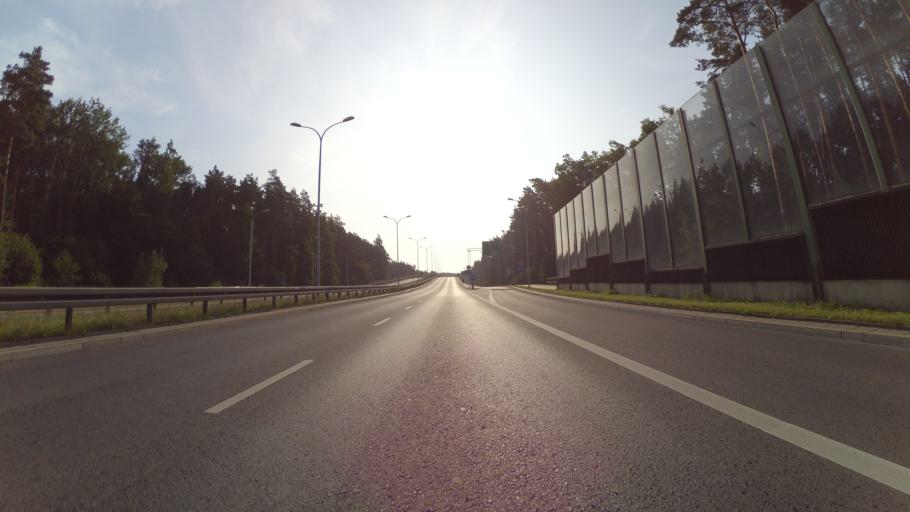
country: PL
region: Podlasie
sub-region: Bialystok
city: Bialystok
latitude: 53.1592
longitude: 23.1375
